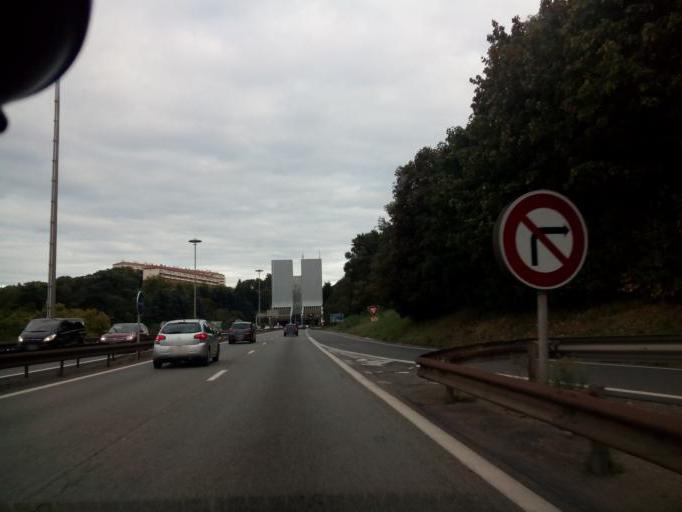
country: FR
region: Rhone-Alpes
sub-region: Departement du Rhone
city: Tassin-la-Demi-Lune
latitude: 45.7659
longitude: 4.7993
